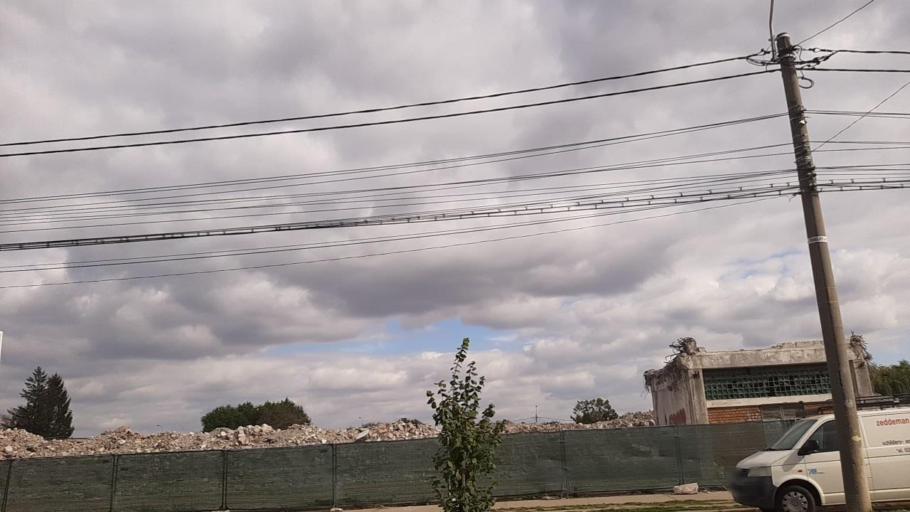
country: RO
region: Galati
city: Galati
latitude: 45.4506
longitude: 28.0349
